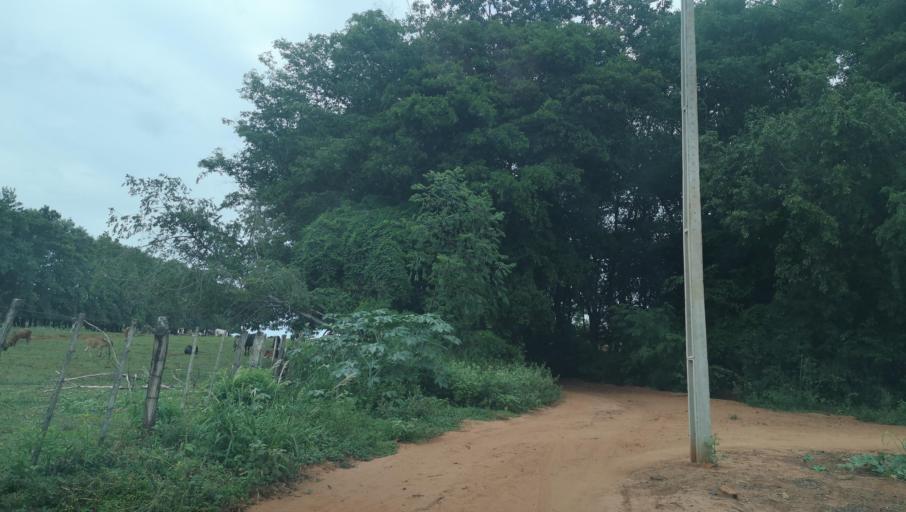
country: PY
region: San Pedro
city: Capiibary
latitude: -24.7365
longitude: -56.0190
